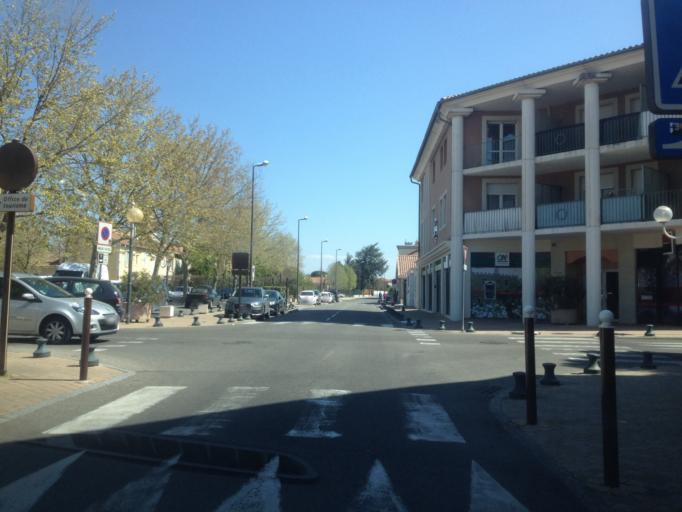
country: FR
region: Provence-Alpes-Cote d'Azur
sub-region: Departement du Vaucluse
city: Le Pontet
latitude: 43.9616
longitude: 4.8598
